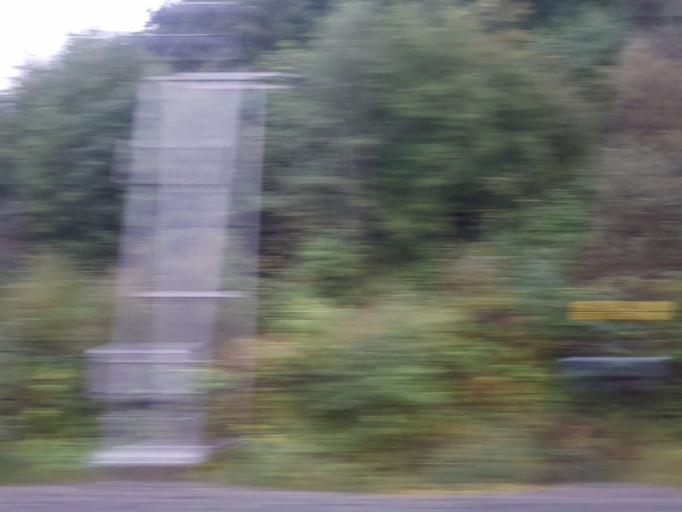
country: NO
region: Sor-Trondelag
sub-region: Melhus
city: Melhus
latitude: 63.2741
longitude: 10.2739
